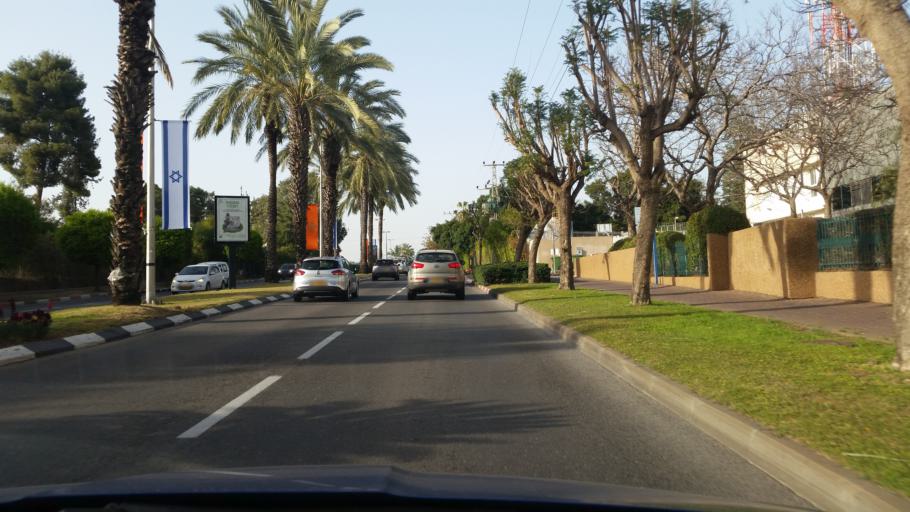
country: IL
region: Central District
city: Ra'anana
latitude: 32.1880
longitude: 34.8548
